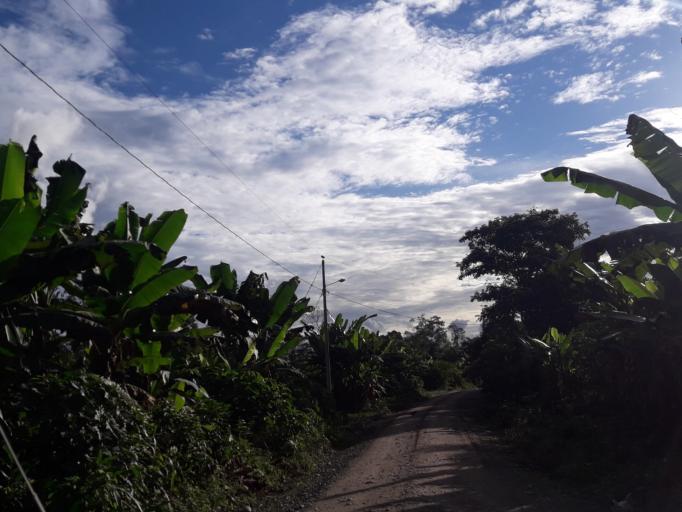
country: EC
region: Orellana
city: Boca Suno
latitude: -0.8834
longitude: -77.2914
